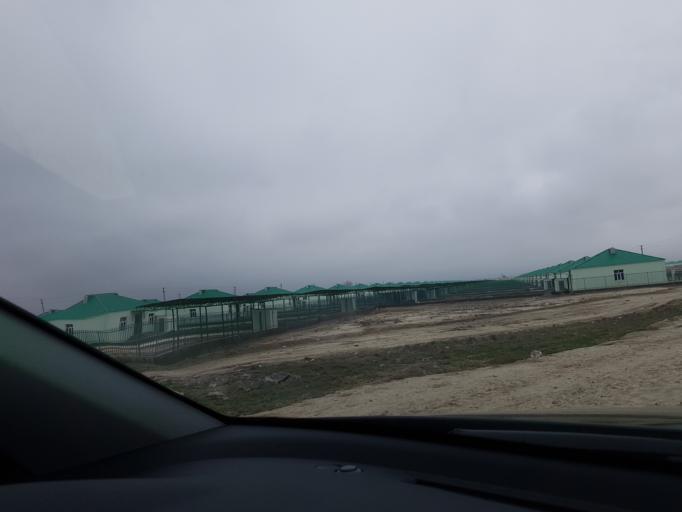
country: TM
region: Ahal
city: Abadan
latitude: 38.1433
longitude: 57.9578
